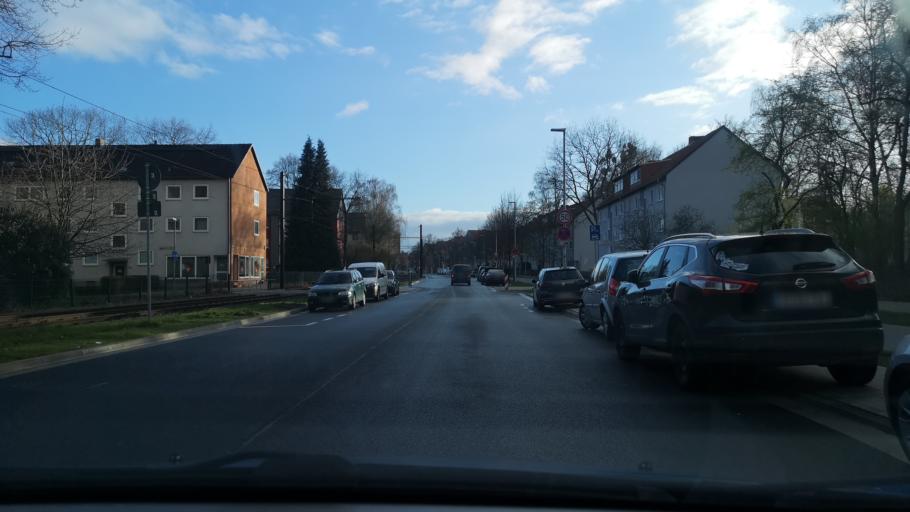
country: DE
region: Lower Saxony
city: Garbsen-Mitte
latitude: 52.4126
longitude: 9.6653
